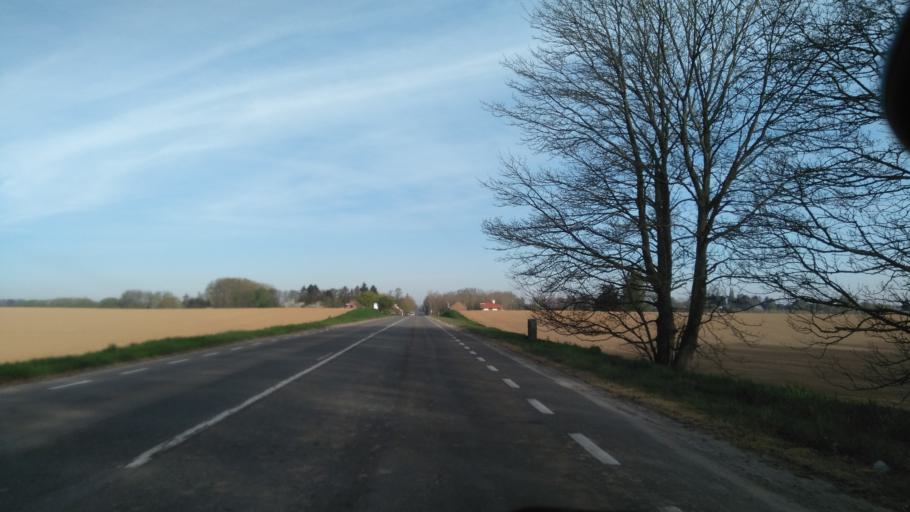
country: BE
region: Wallonia
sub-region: Province de Namur
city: Eghezee
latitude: 50.6025
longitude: 4.9006
